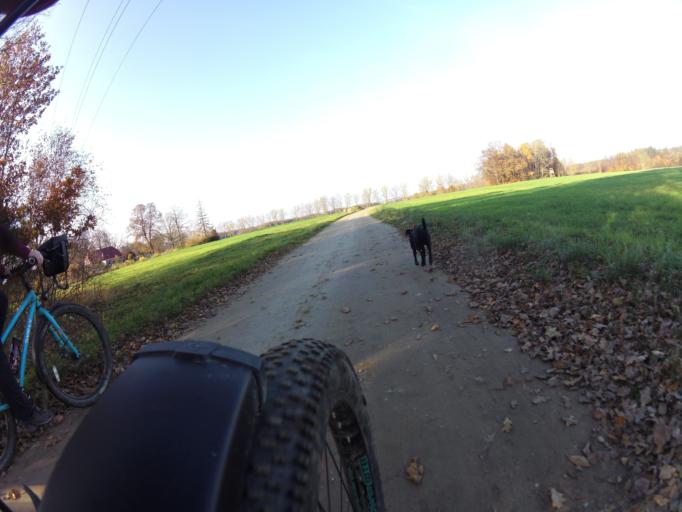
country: PL
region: Pomeranian Voivodeship
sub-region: Powiat pucki
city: Krokowa
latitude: 54.7323
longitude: 18.1974
